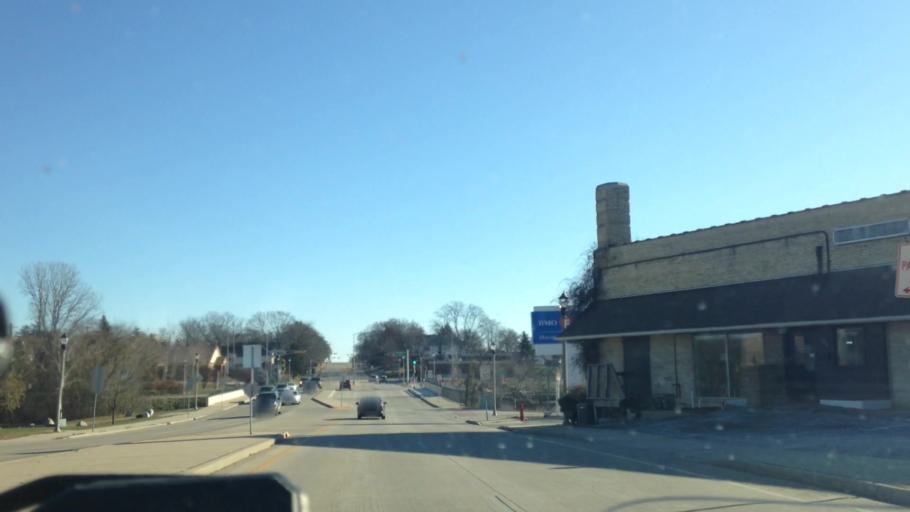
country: US
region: Wisconsin
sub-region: Washington County
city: West Bend
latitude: 43.4268
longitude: -88.1841
